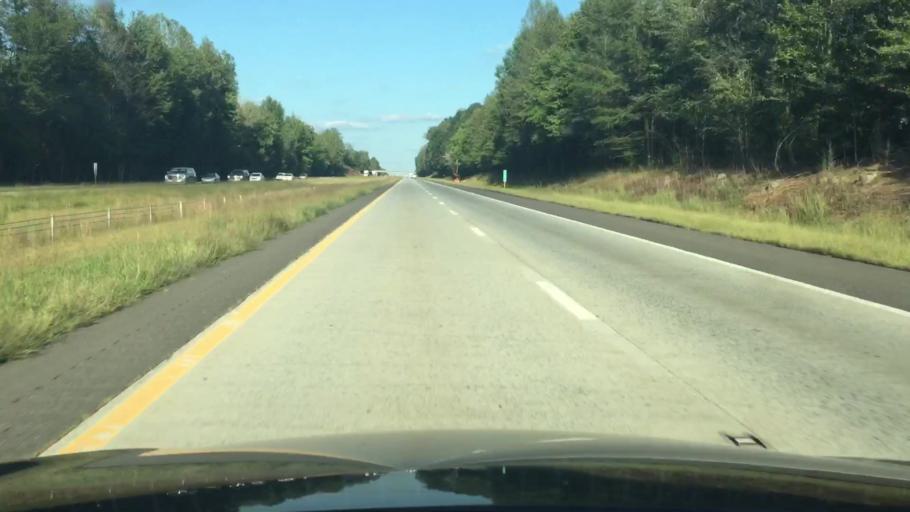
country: US
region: North Carolina
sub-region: Davie County
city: Mocksville
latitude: 35.8822
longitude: -80.6810
